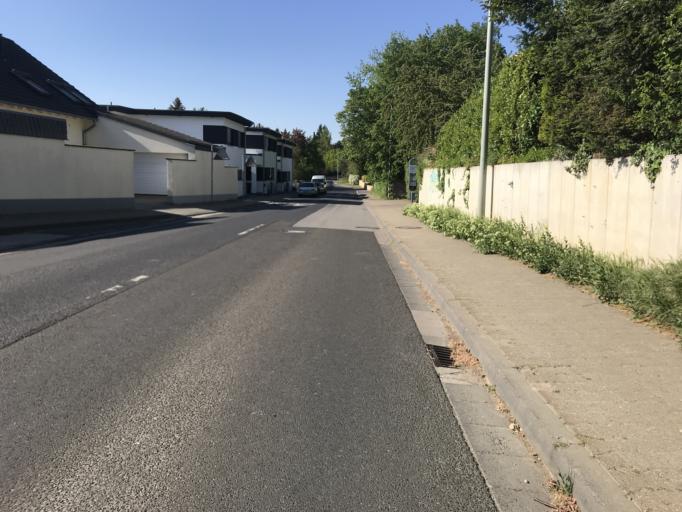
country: DE
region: Rheinland-Pfalz
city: Zornheim
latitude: 49.8913
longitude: 8.2249
